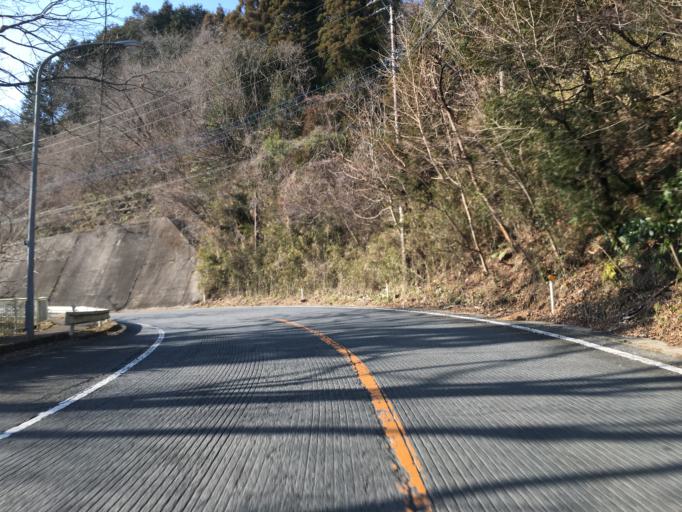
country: JP
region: Ibaraki
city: Takahagi
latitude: 36.7255
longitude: 140.6389
